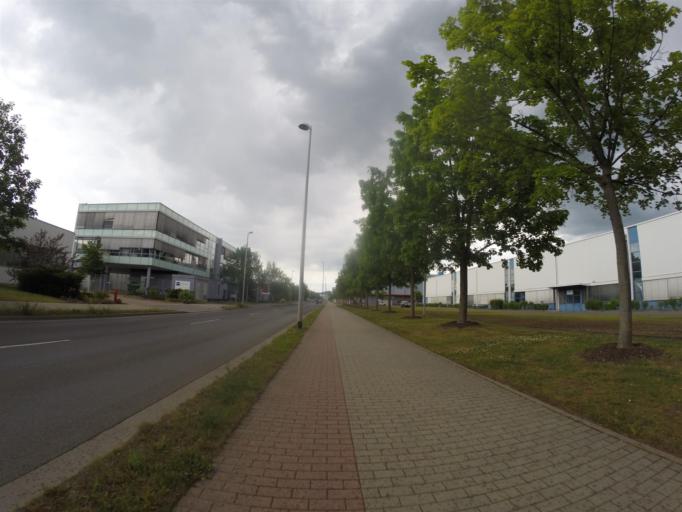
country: DE
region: Thuringia
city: Sulza
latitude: 50.8852
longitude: 11.5964
